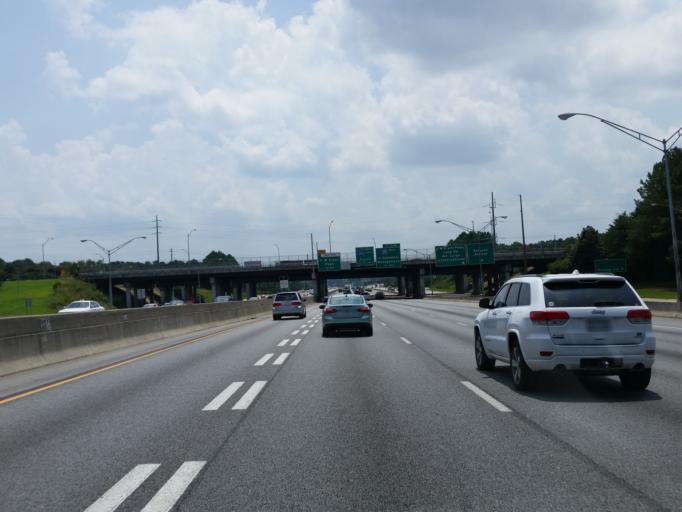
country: US
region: Georgia
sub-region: Fulton County
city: Hapeville
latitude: 33.6545
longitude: -84.3955
